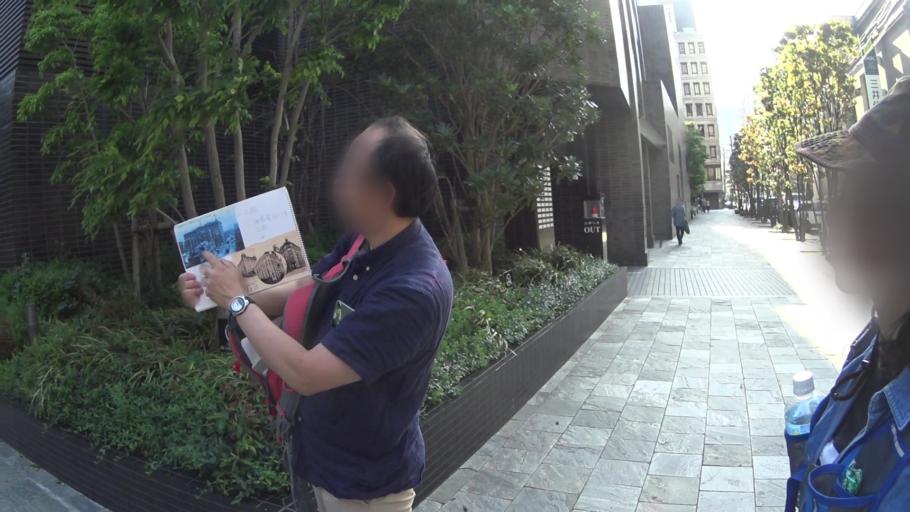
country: JP
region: Osaka
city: Osaka-shi
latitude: 34.6895
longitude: 135.5073
